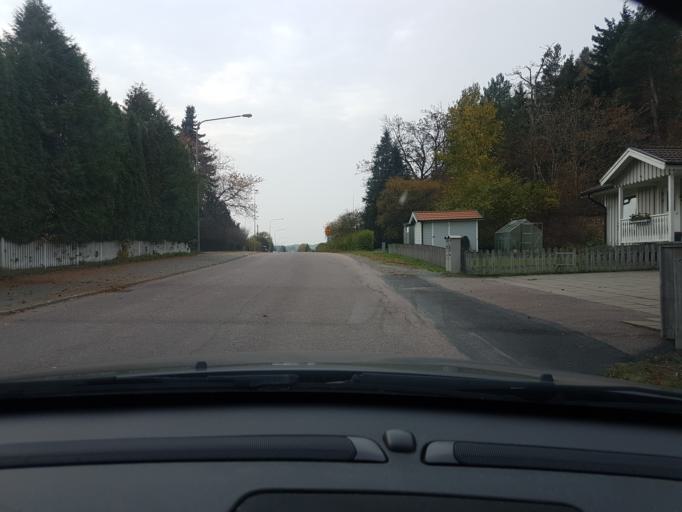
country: SE
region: Vaestra Goetaland
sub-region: Ale Kommun
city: Alvangen
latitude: 57.9519
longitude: 12.1098
